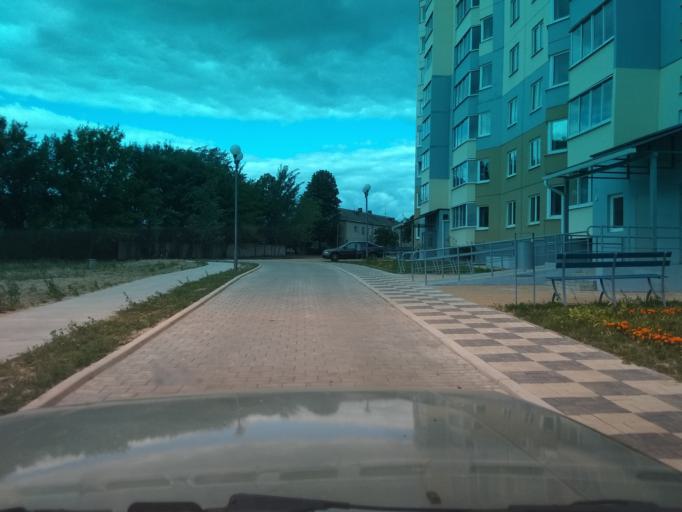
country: BY
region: Mogilev
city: Mahilyow
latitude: 53.9227
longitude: 30.3543
